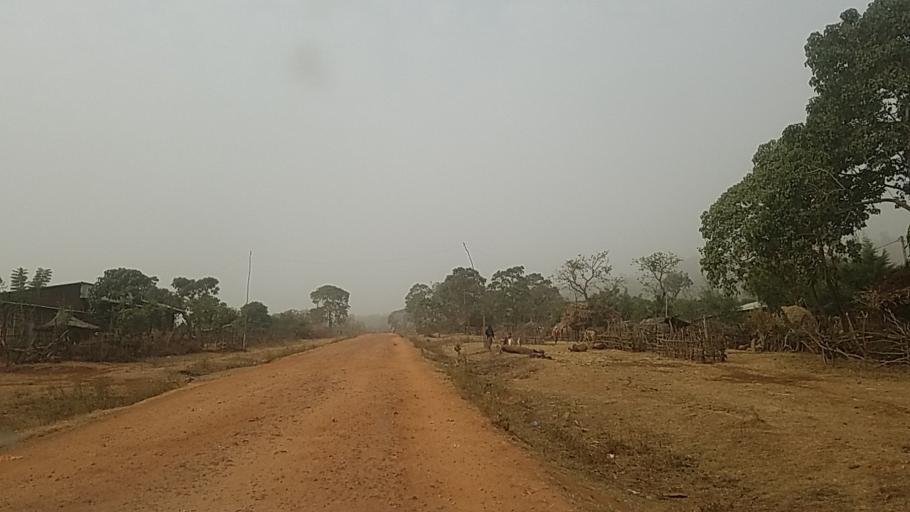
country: ET
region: Amhara
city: Bure
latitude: 10.8613
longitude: 36.3888
